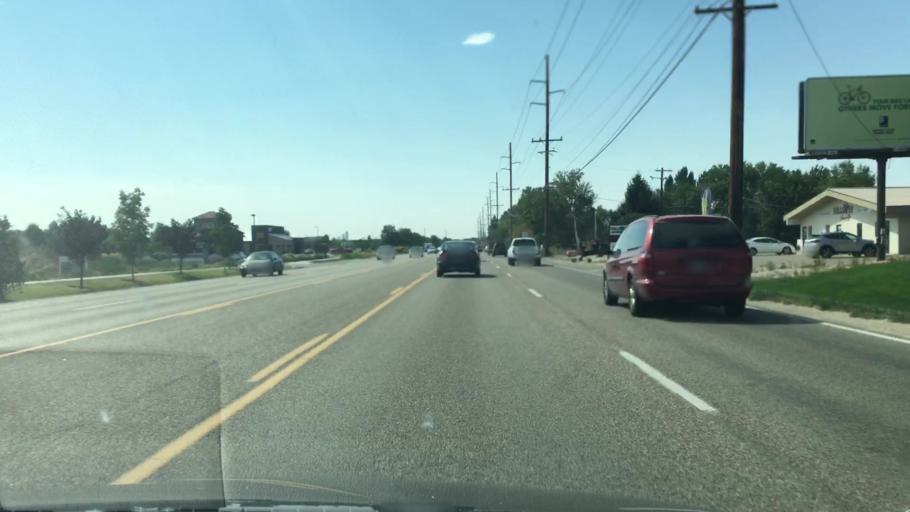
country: US
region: Idaho
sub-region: Ada County
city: Eagle
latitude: 43.6800
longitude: -116.3064
